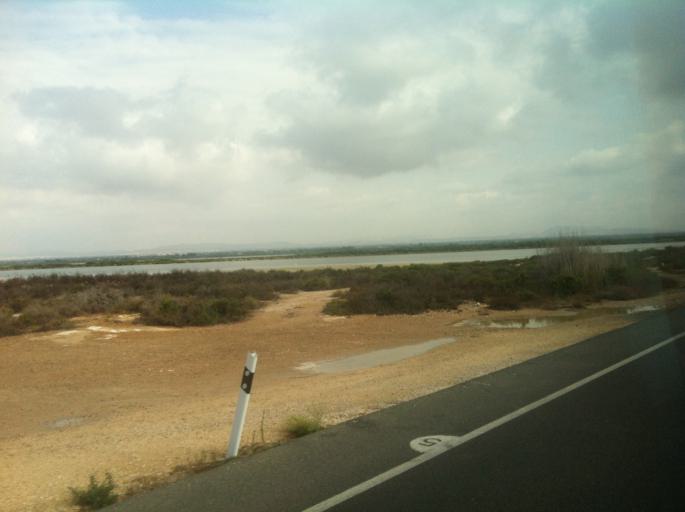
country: ES
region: Valencia
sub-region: Provincia de Alicante
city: Santa Pola
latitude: 38.1803
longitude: -0.6183
